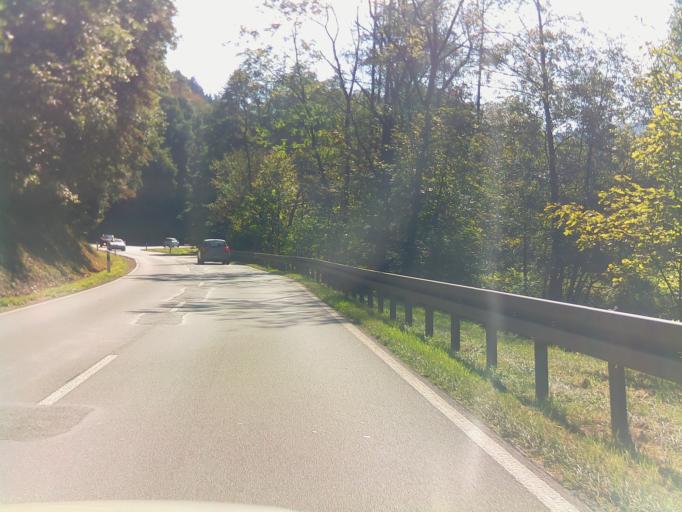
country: DE
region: Thuringia
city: Leutenberg
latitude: 50.5853
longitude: 11.4398
